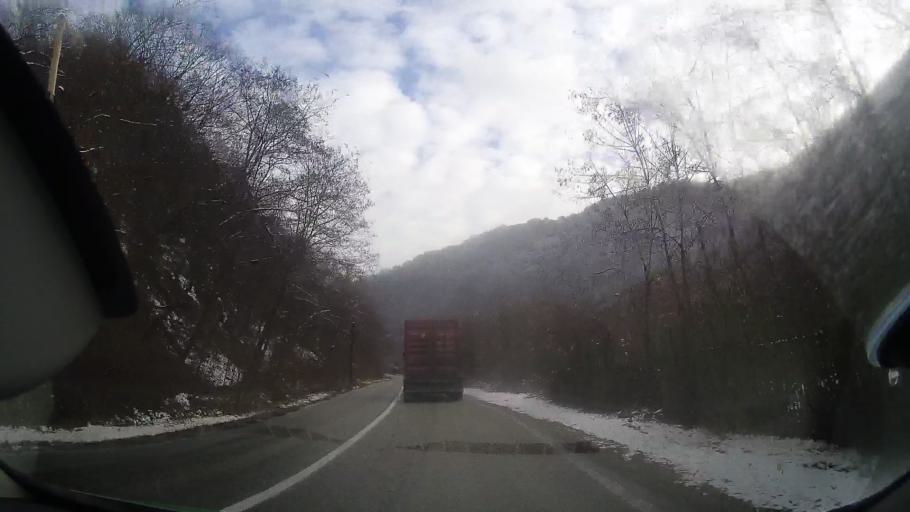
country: RO
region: Alba
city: Salciua de Sus
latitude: 46.4022
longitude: 23.3484
